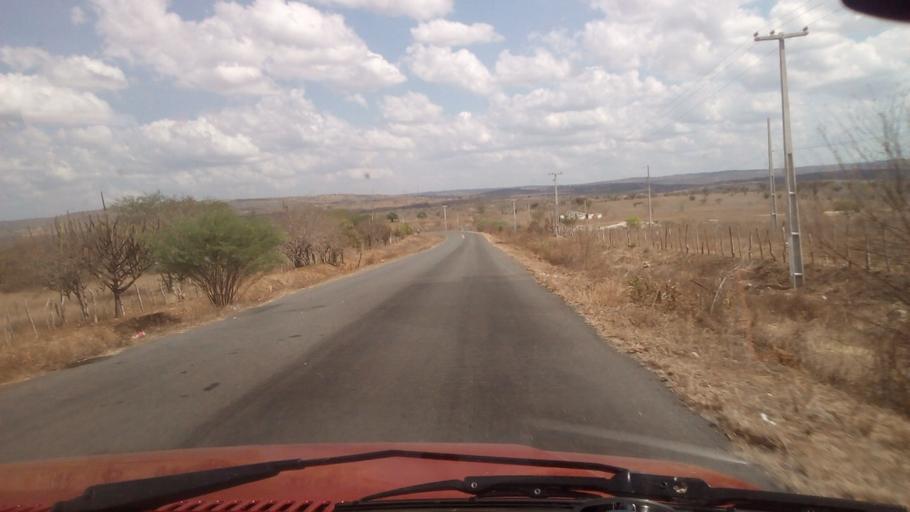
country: BR
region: Paraiba
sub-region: Cacimba De Dentro
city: Cacimba de Dentro
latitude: -6.6723
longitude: -35.7523
